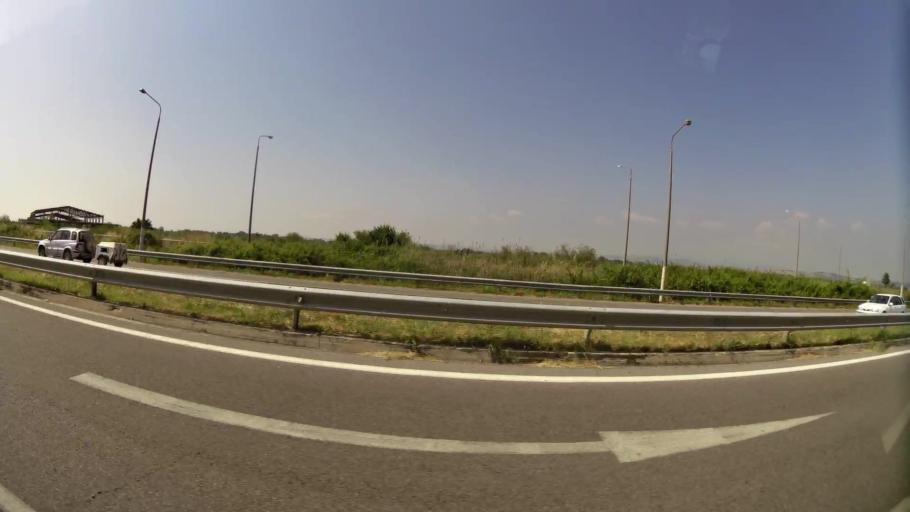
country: GR
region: Central Macedonia
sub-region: Nomos Imathias
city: Kleidi
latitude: 40.5590
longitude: 22.5887
